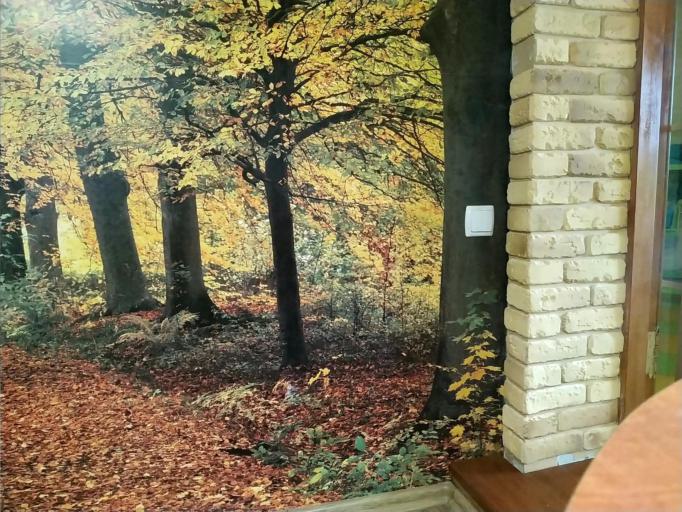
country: BY
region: Mogilev
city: Khotsimsk
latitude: 53.5522
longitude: 32.5189
